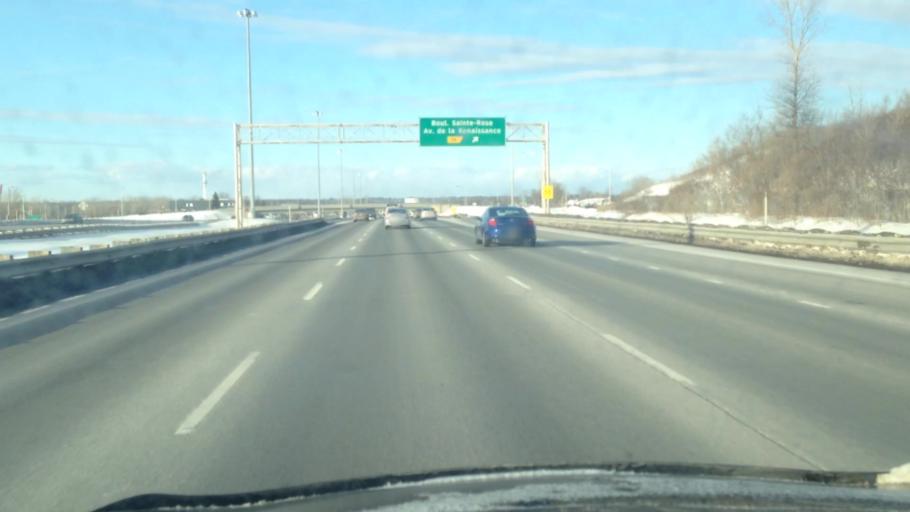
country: CA
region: Quebec
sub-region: Laurentides
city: Boisbriand
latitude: 45.5962
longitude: -73.8033
